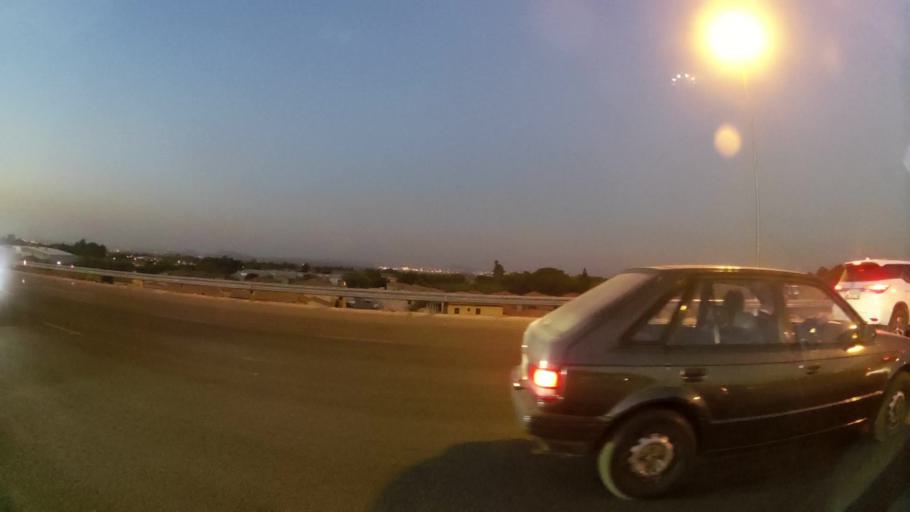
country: ZA
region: North-West
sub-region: Bojanala Platinum District Municipality
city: Rustenburg
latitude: -25.6992
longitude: 27.2547
